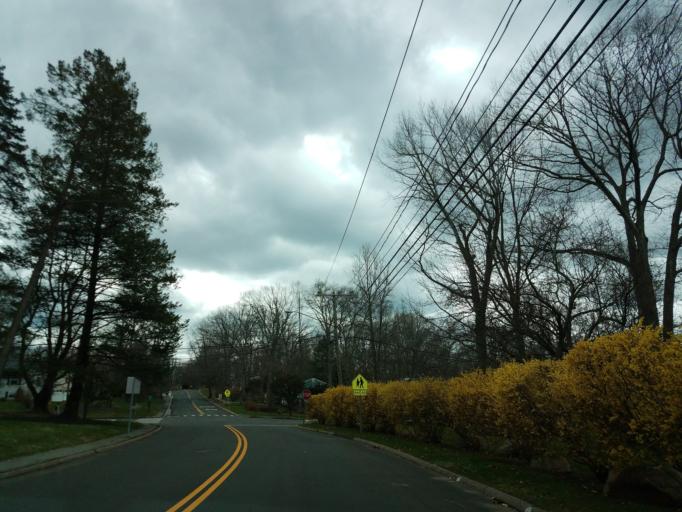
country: US
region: Connecticut
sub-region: Fairfield County
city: Stamford
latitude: 41.0932
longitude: -73.5413
